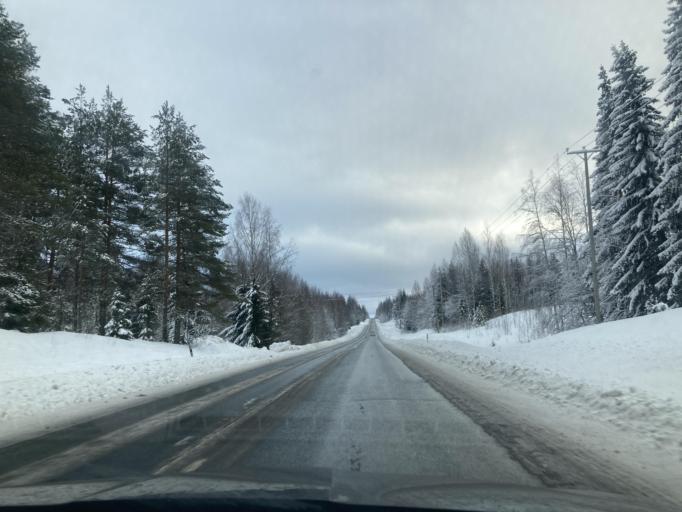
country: FI
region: Paijanne Tavastia
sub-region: Lahti
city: Padasjoki
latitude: 61.2801
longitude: 25.3208
